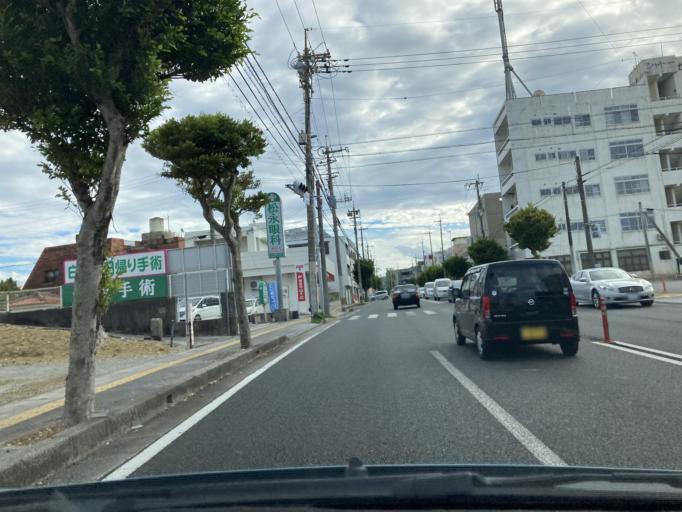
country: JP
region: Okinawa
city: Okinawa
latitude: 26.3448
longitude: 127.8136
